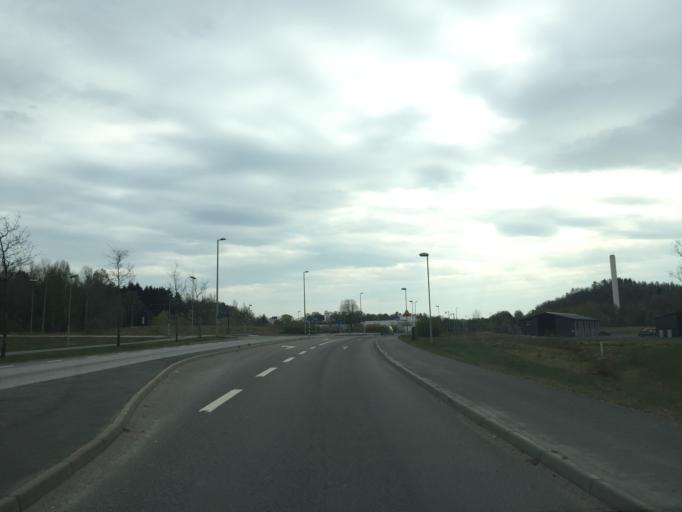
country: SE
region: Vaestra Goetaland
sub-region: Goteborg
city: Loevgaerdet
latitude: 57.8061
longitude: 12.0433
